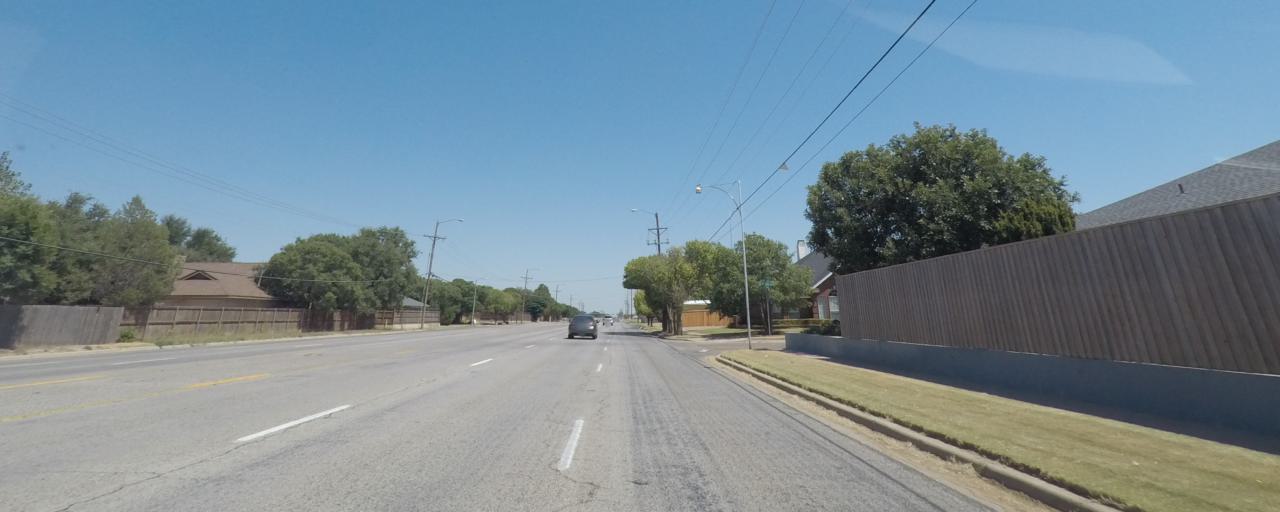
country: US
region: Texas
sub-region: Lubbock County
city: Lubbock
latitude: 33.5052
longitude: -101.8937
